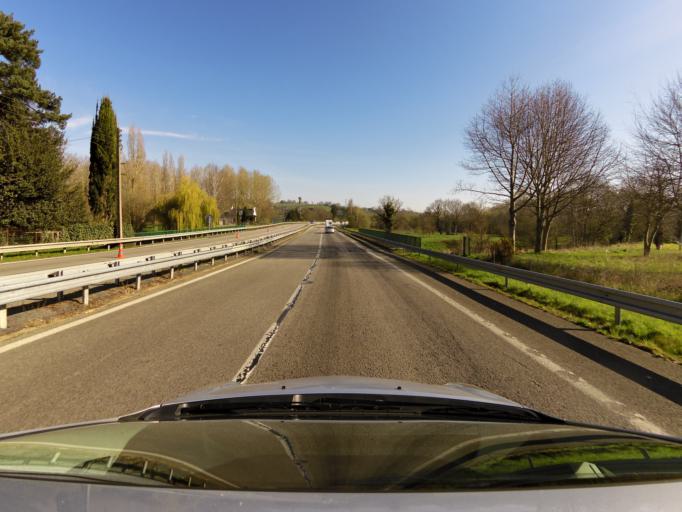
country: FR
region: Brittany
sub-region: Departement du Morbihan
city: Guegon
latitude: 47.9518
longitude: -2.5757
